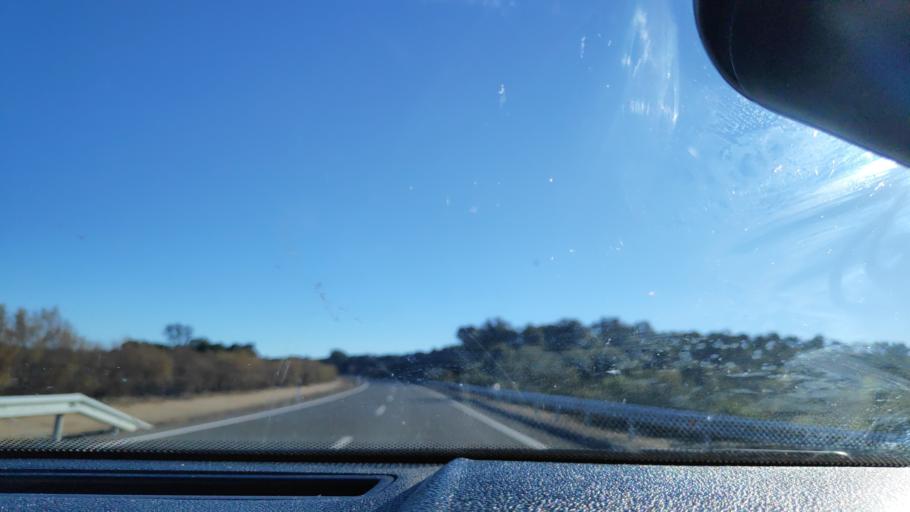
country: ES
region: Extremadura
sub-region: Provincia de Badajoz
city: Monesterio
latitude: 38.1062
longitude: -6.2717
